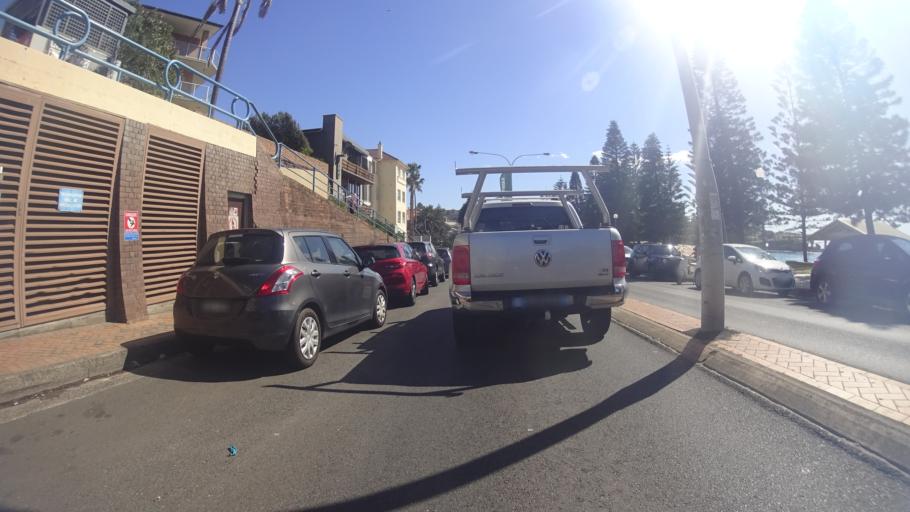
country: AU
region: New South Wales
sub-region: Randwick
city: Coogee
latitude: -33.9222
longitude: 151.2565
